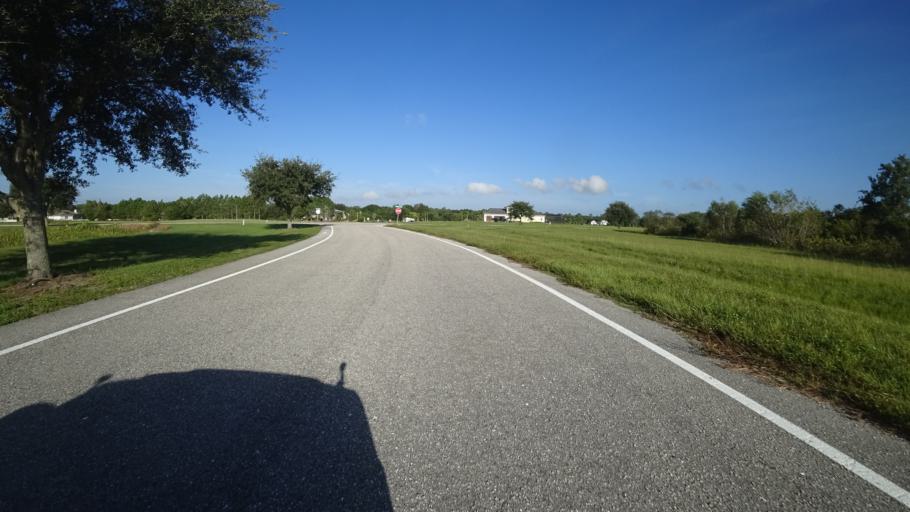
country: US
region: Florida
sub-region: Hillsborough County
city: Sun City Center
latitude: 27.5699
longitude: -82.3542
